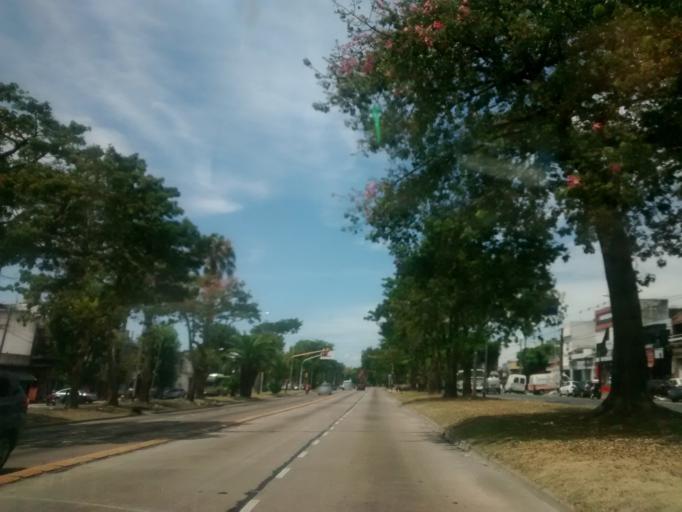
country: AR
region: Buenos Aires
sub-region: Partido de Avellaneda
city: Avellaneda
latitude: -34.6844
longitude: -58.3423
